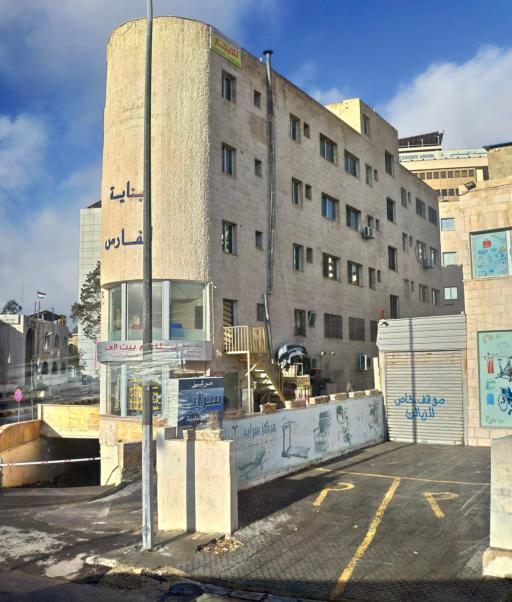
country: JO
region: Amman
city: Amman
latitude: 31.9692
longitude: 35.9086
